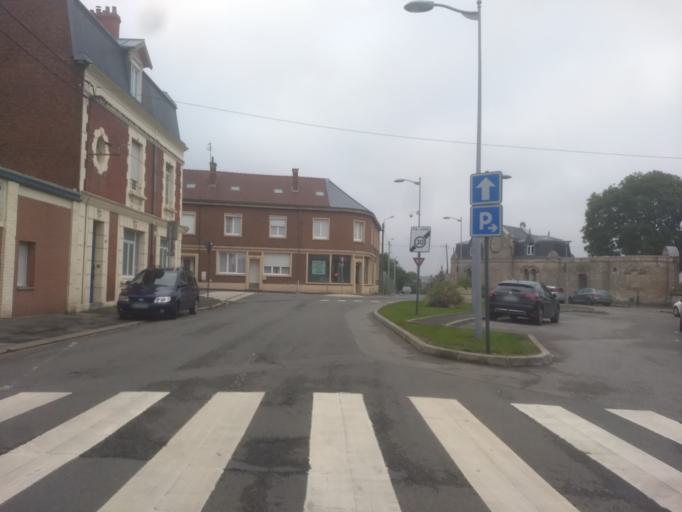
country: FR
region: Nord-Pas-de-Calais
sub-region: Departement du Pas-de-Calais
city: Arras
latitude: 50.2890
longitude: 2.7936
